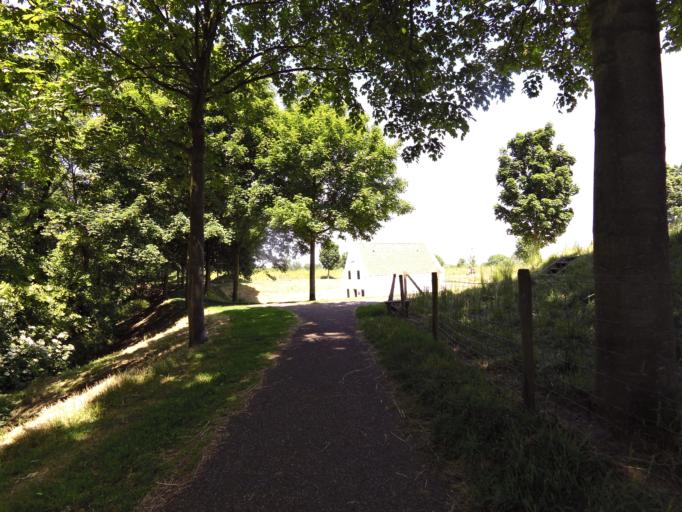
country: NL
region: South Holland
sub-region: Gemeente Brielle
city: Brielle
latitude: 51.9037
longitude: 4.1703
